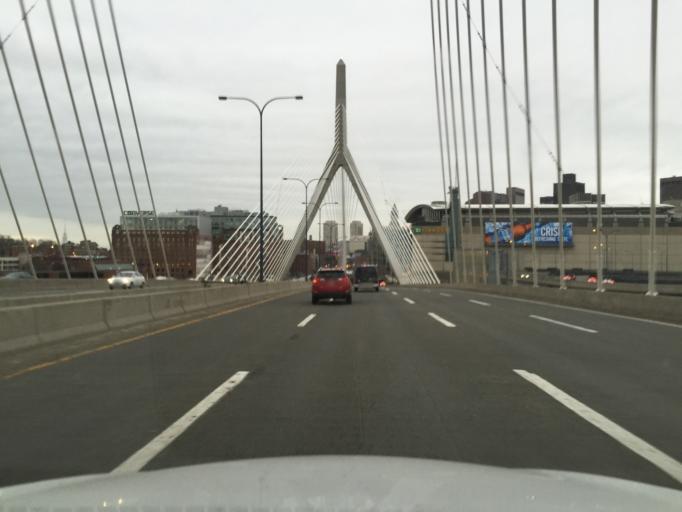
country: US
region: Massachusetts
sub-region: Suffolk County
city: Boston
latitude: 42.3694
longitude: -71.0642
